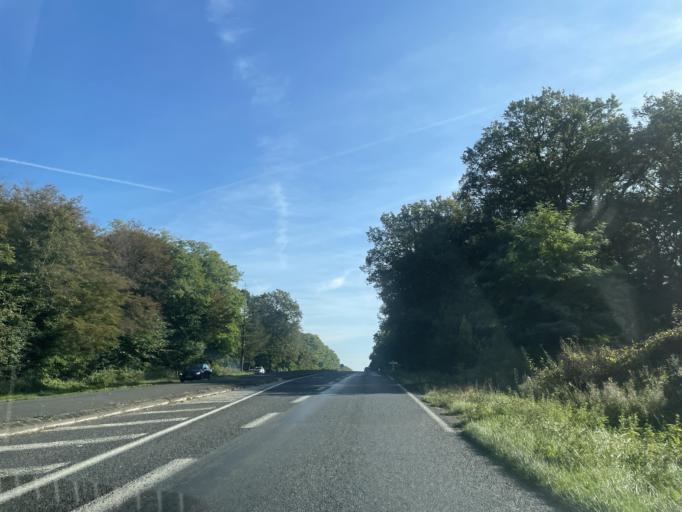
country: FR
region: Ile-de-France
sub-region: Departement de Seine-et-Marne
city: Trilport
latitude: 48.9588
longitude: 2.9829
